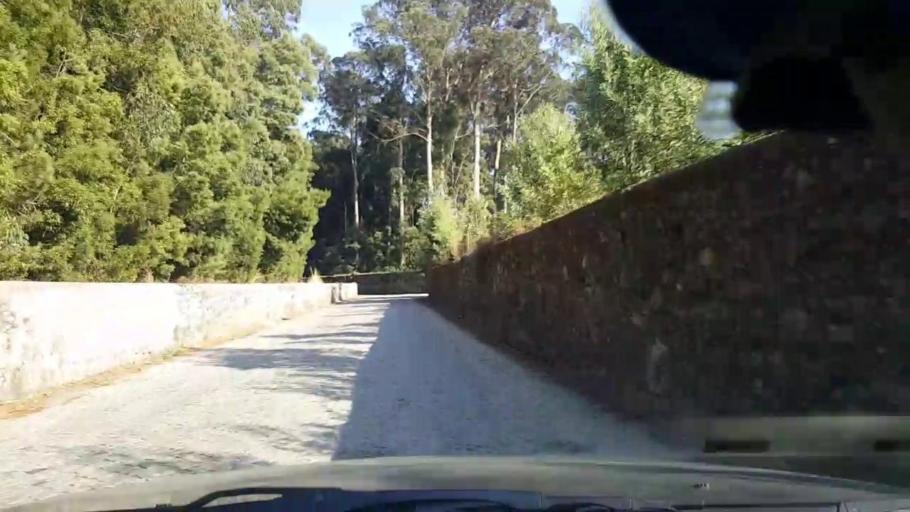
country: PT
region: Porto
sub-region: Vila do Conde
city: Arvore
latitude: 41.3467
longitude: -8.6906
